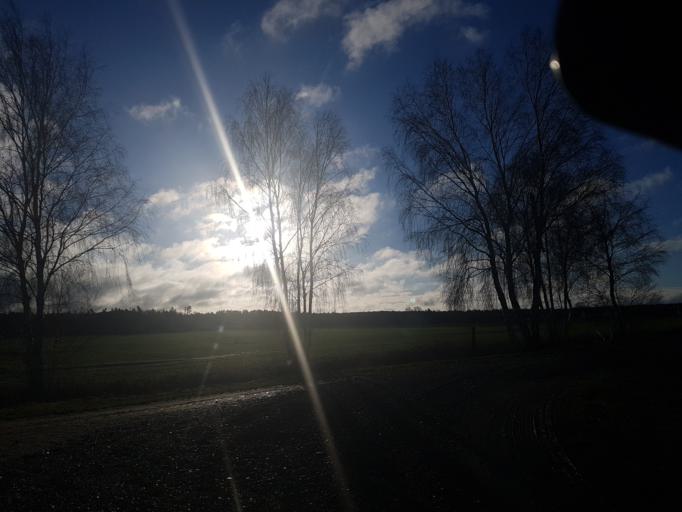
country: DE
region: Brandenburg
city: Schonborn
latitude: 51.5479
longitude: 13.4721
